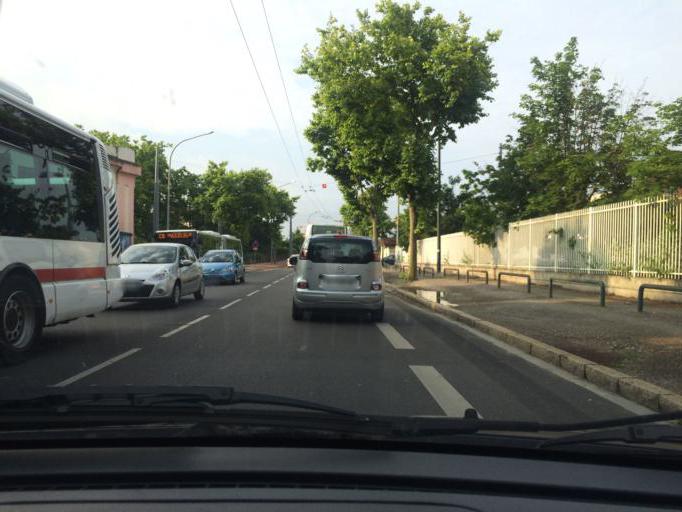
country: FR
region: Rhone-Alpes
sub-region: Departement du Rhone
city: Vaulx-en-Velin
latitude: 45.7598
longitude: 4.9208
